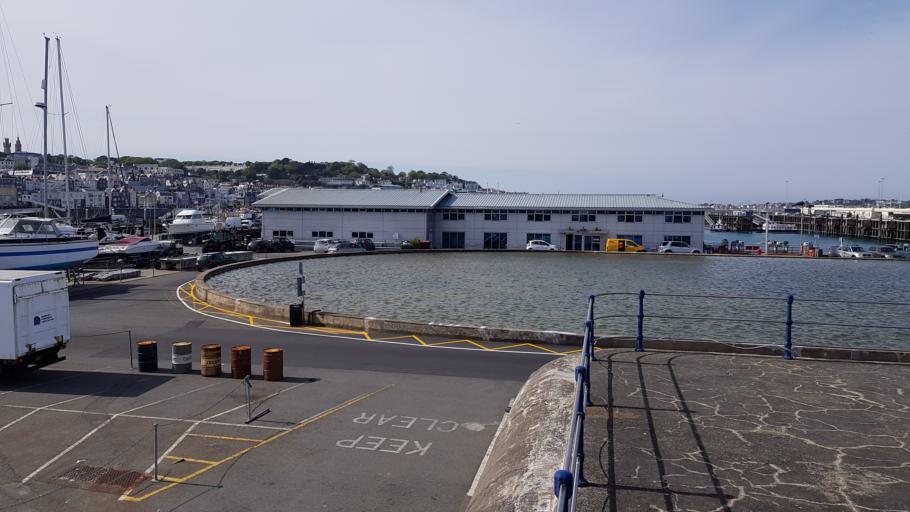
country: GG
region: St Peter Port
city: Saint Peter Port
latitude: 49.4531
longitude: -2.5301
